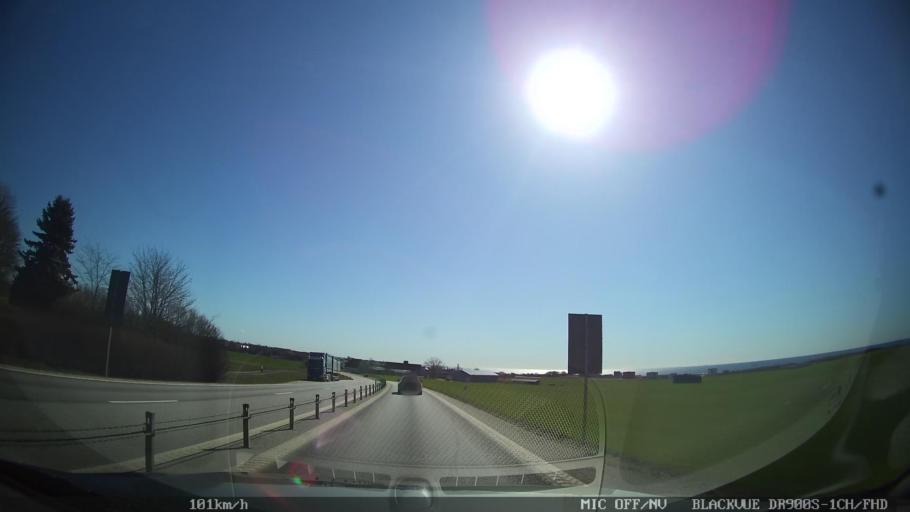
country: SE
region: Skane
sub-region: Ystads Kommun
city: Ystad
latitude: 55.4426
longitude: 13.7809
